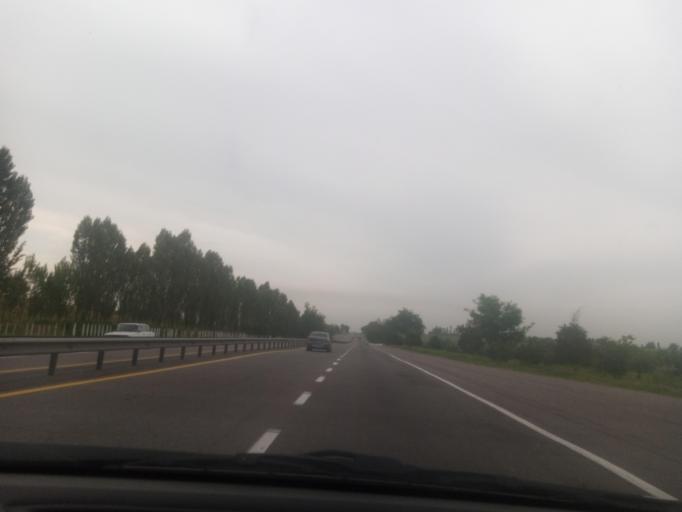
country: UZ
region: Toshkent
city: Tuytepa
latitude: 41.0907
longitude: 69.4628
